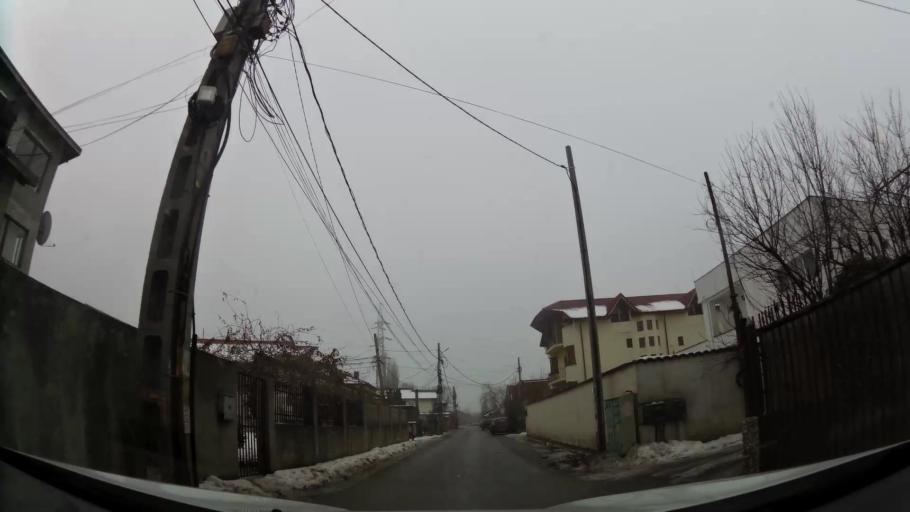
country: RO
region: Ilfov
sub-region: Comuna Chiajna
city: Rosu
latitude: 44.4470
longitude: 26.0051
